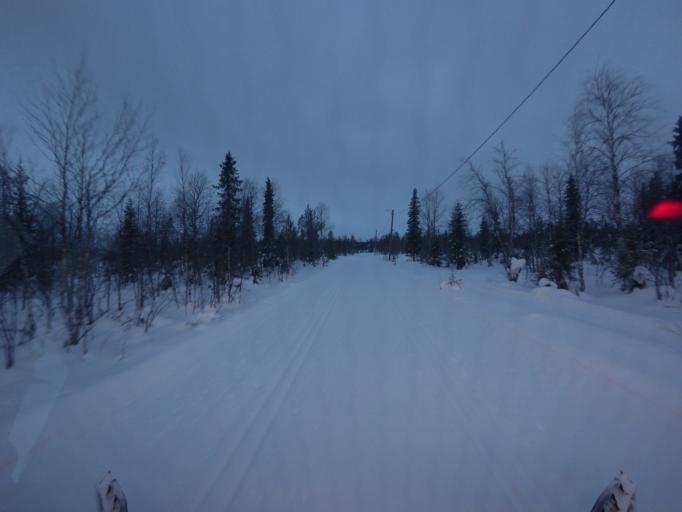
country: FI
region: Lapland
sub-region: Tunturi-Lappi
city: Kolari
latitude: 67.6145
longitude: 24.1655
